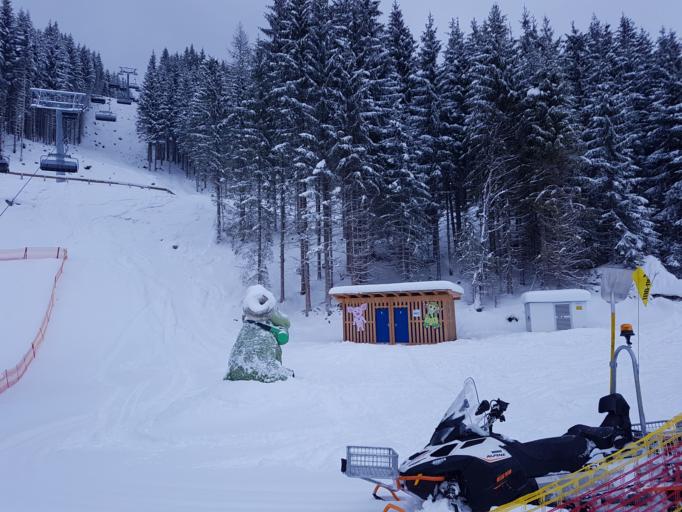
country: AT
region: Salzburg
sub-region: Politischer Bezirk Sankt Johann im Pongau
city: Kleinarl
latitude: 47.2908
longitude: 13.3215
